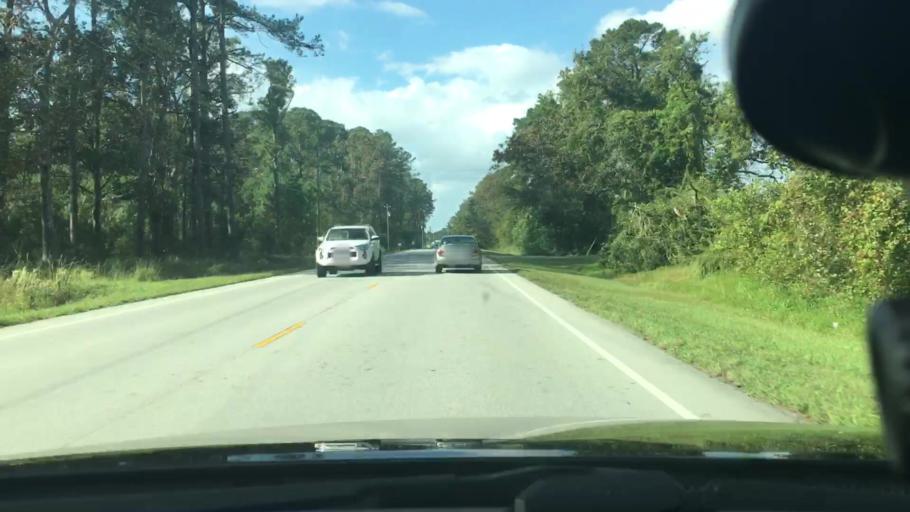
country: US
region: North Carolina
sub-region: Craven County
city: New Bern
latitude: 35.2129
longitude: -77.0624
